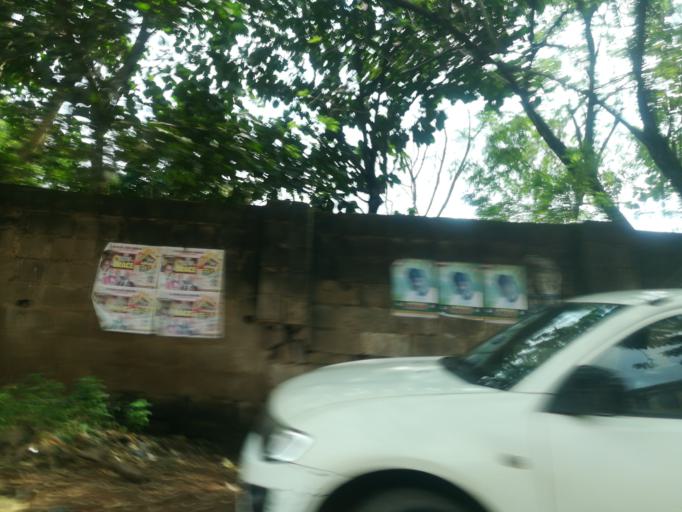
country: NG
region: Oyo
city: Ibadan
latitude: 7.3622
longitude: 3.8829
